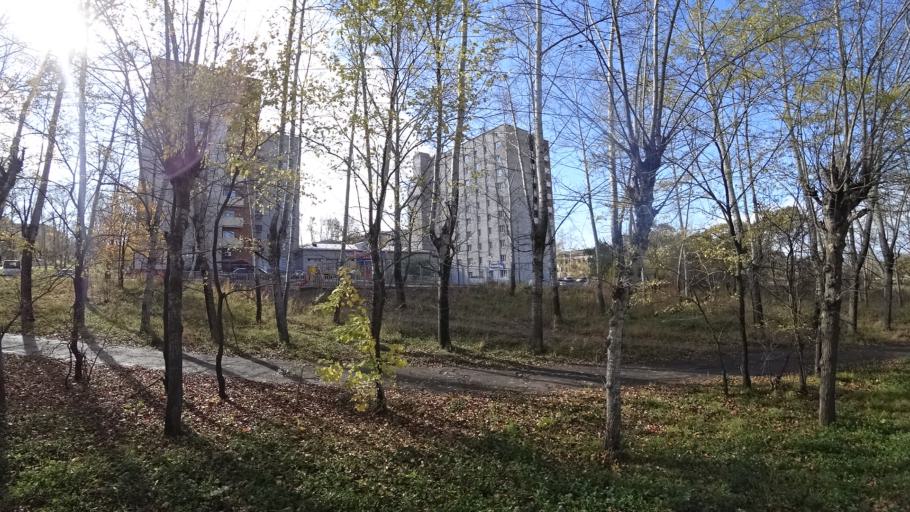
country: RU
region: Khabarovsk Krai
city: Amursk
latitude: 50.2225
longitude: 136.9025
